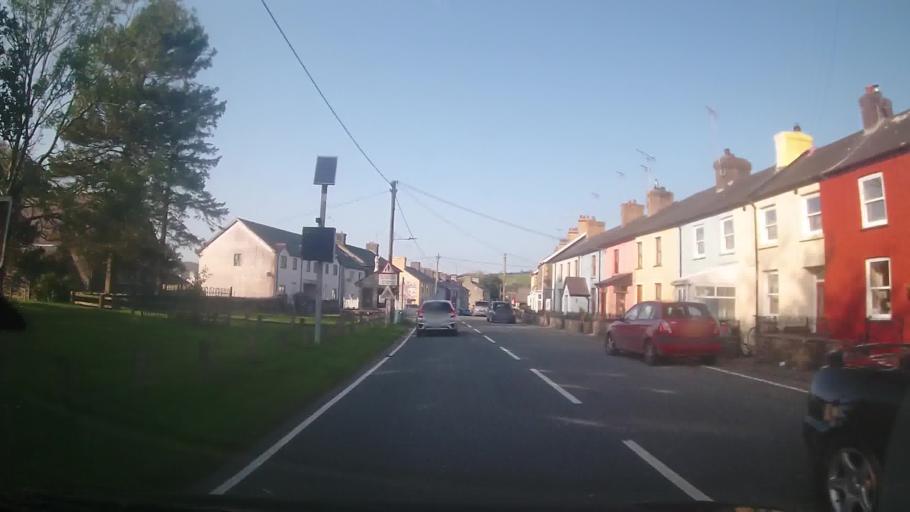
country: GB
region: Wales
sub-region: County of Ceredigion
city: Lledrod
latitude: 52.2803
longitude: -3.8635
